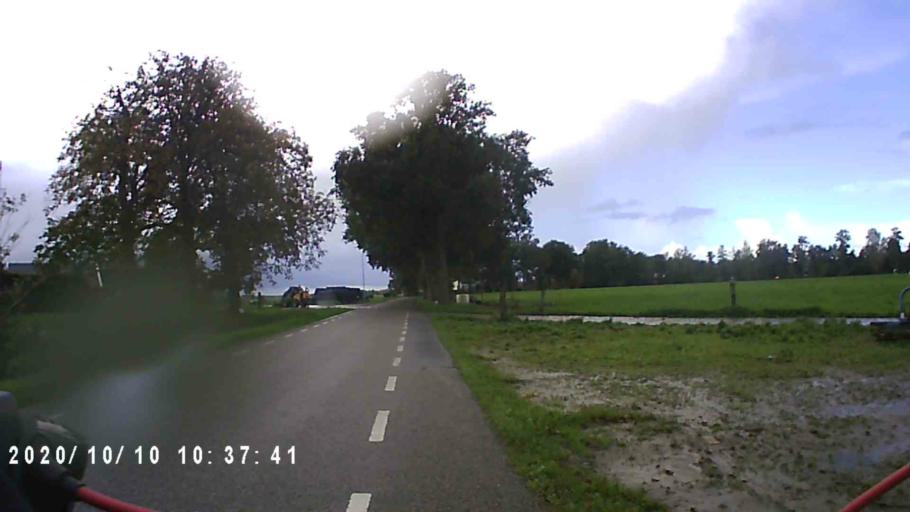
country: NL
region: Groningen
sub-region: Gemeente Grootegast
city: Grootegast
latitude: 53.1828
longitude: 6.2991
